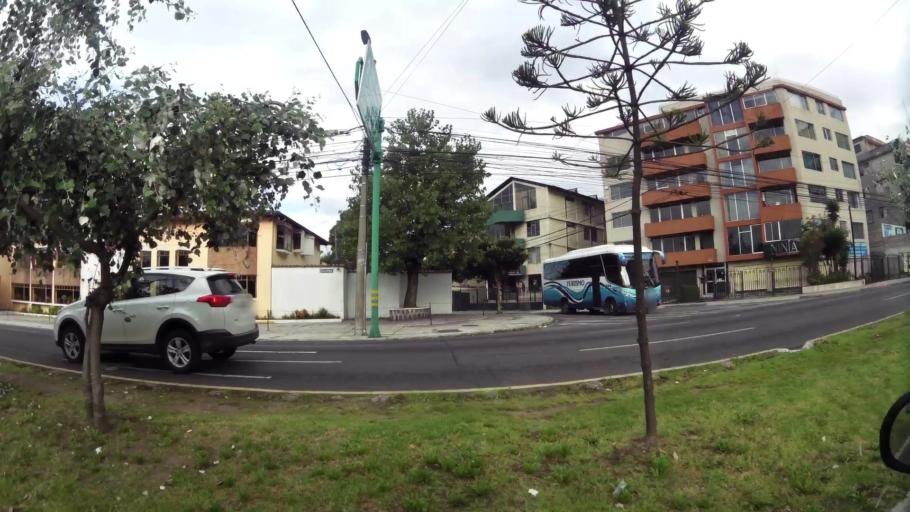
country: EC
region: Pichincha
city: Quito
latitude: -0.1871
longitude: -78.4878
